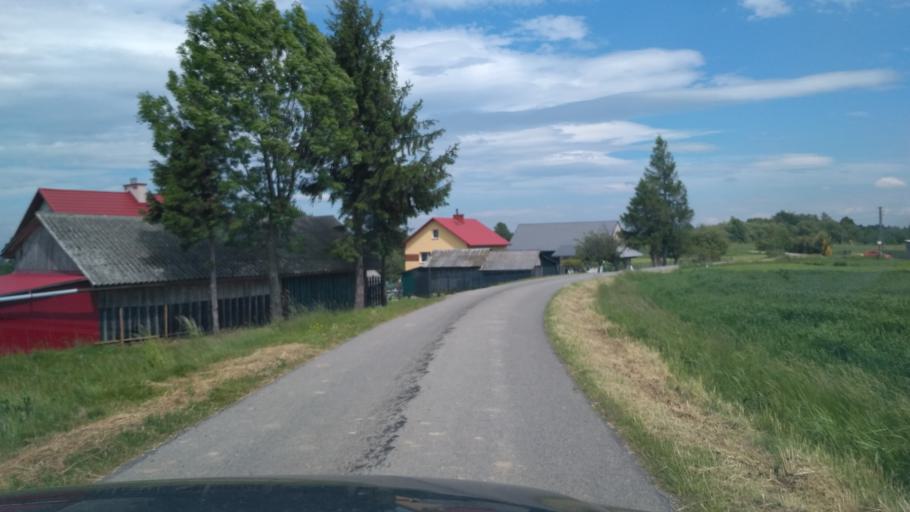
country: PL
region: Subcarpathian Voivodeship
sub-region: Powiat ropczycko-sedziszowski
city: Wielopole Skrzynskie
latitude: 49.9744
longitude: 21.6474
